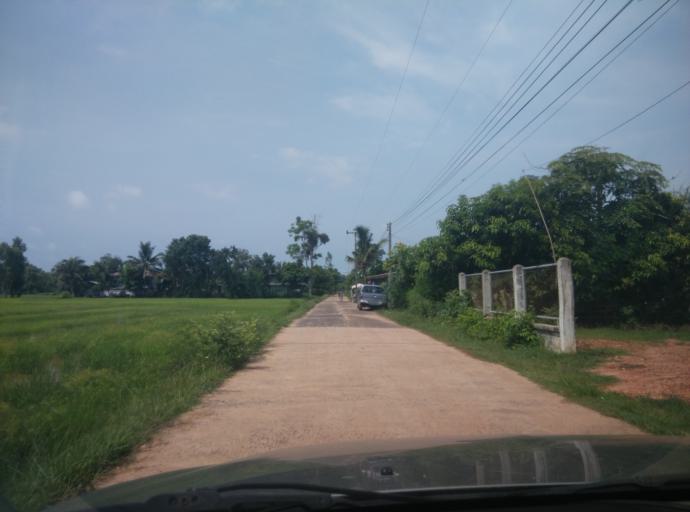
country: TH
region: Sisaket
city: Huai Thap Than
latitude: 15.0501
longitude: 104.0825
